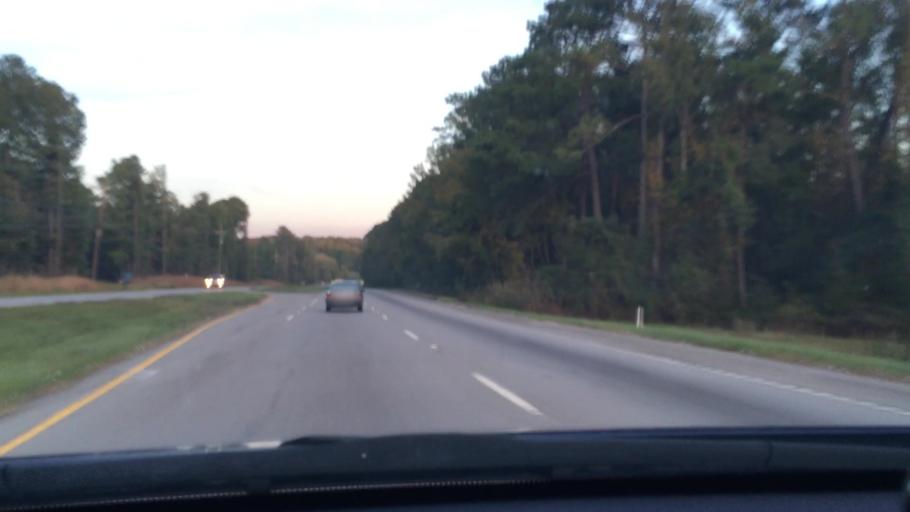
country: US
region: South Carolina
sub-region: Richland County
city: Hopkins
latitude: 33.9521
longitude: -80.8338
